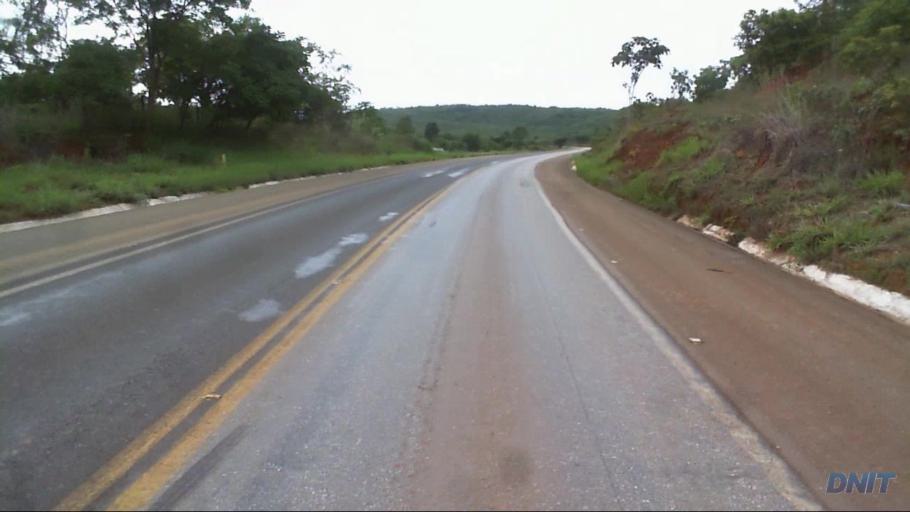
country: BR
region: Goias
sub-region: Barro Alto
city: Barro Alto
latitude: -14.9273
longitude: -48.9489
